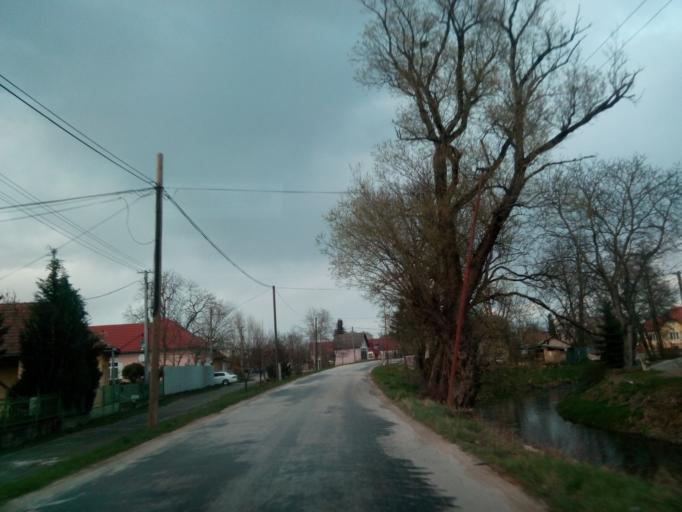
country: SK
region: Kosicky
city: Moldava nad Bodvou
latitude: 48.5869
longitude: 20.9893
